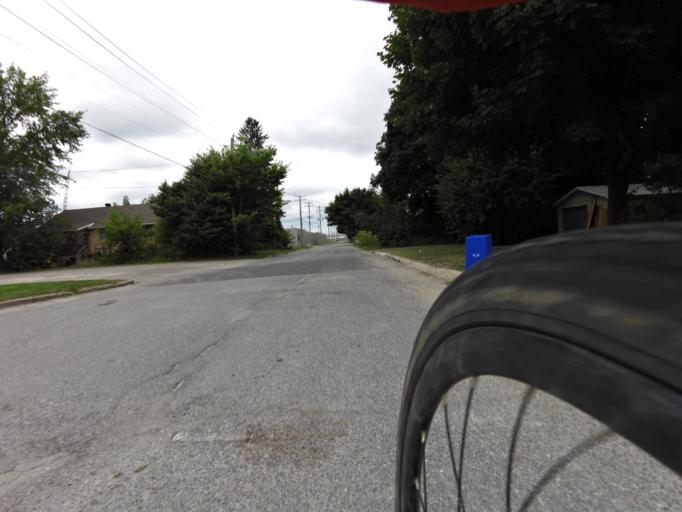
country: CA
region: Ontario
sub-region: Lanark County
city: Smiths Falls
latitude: 44.9011
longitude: -76.0264
